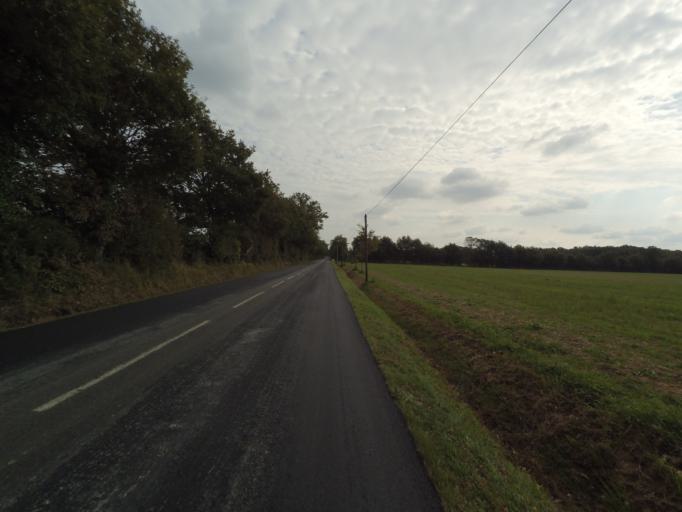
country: FR
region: Pays de la Loire
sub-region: Departement de la Vendee
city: Saint-Hilaire-de-Loulay
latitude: 46.9917
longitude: -1.3664
